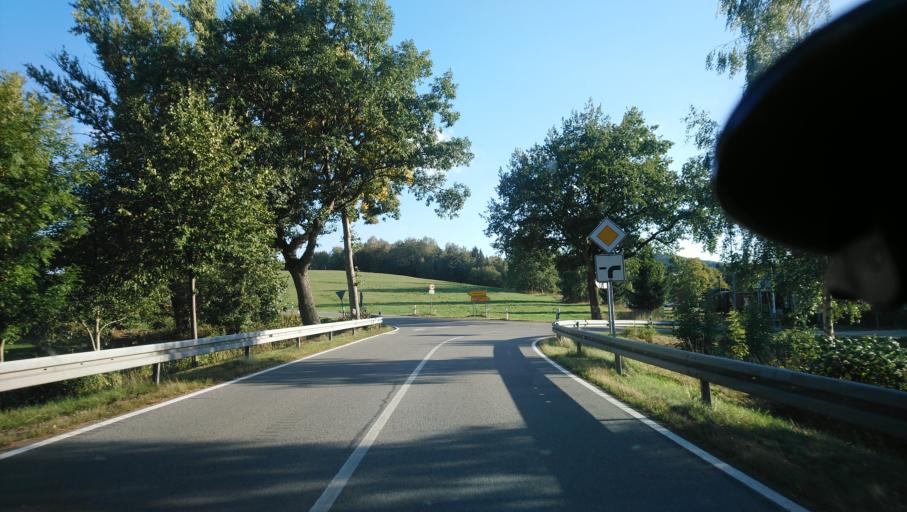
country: DE
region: Saxony
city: Schlettau
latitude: 50.5470
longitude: 12.9648
